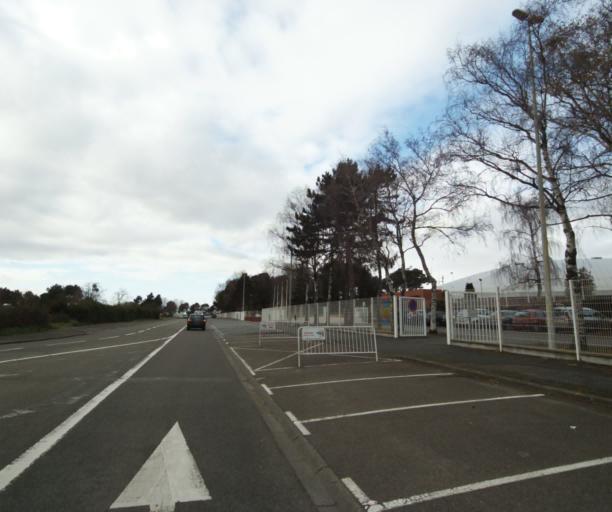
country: FR
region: Pays de la Loire
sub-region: Departement de la Sarthe
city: Arnage
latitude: 47.9569
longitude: 0.2024
